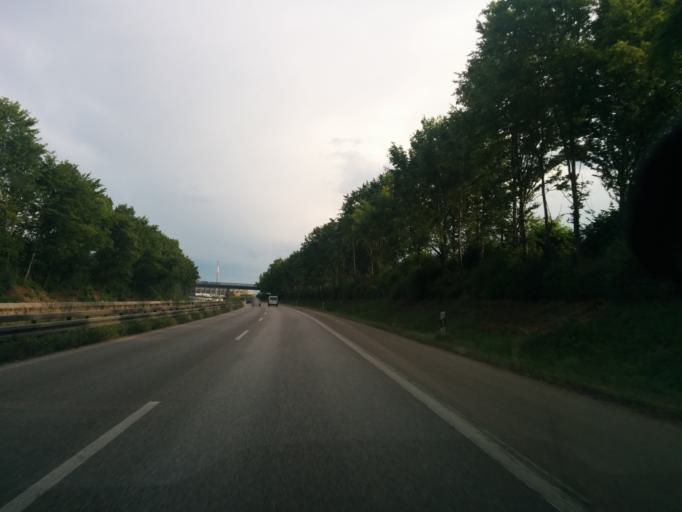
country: DE
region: Bavaria
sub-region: Swabia
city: Augsburg
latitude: 48.3330
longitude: 10.8872
